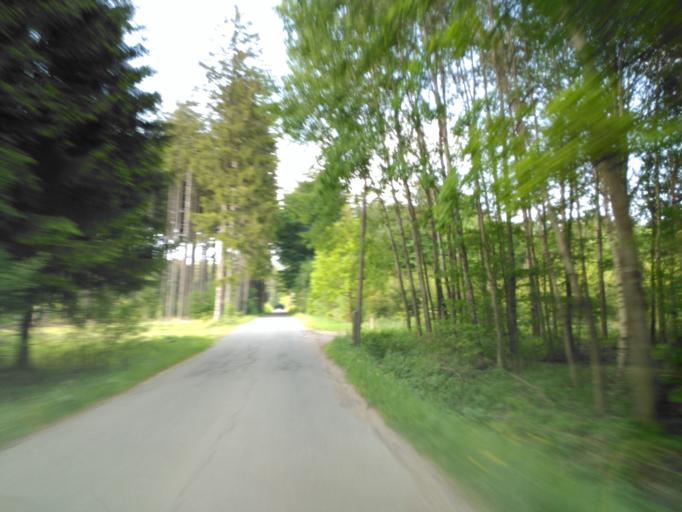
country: CZ
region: Plzensky
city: Zbiroh
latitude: 49.8972
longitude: 13.8097
